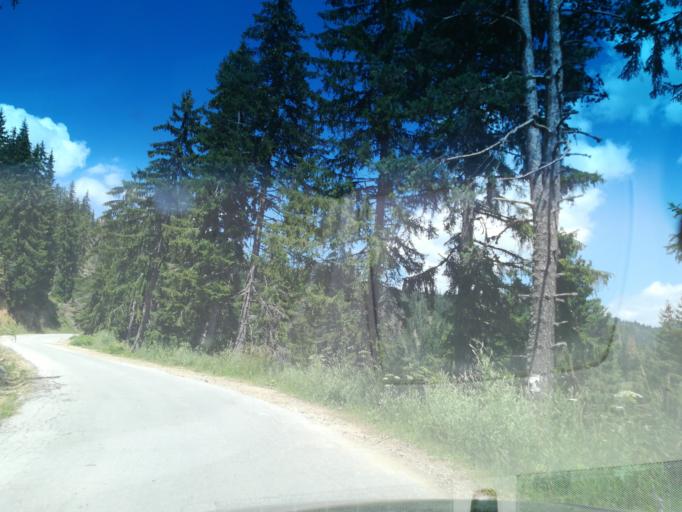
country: BG
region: Smolyan
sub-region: Obshtina Chepelare
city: Chepelare
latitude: 41.6832
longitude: 24.7699
